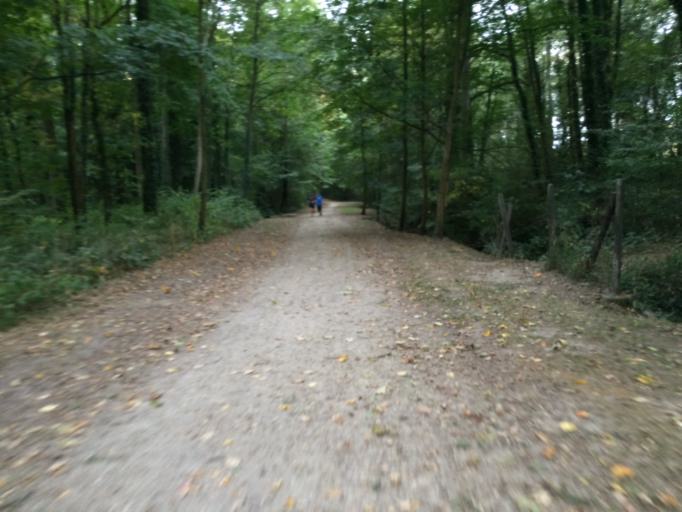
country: FR
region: Ile-de-France
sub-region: Departement de l'Essonne
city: Linas
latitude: 48.6369
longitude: 2.2518
